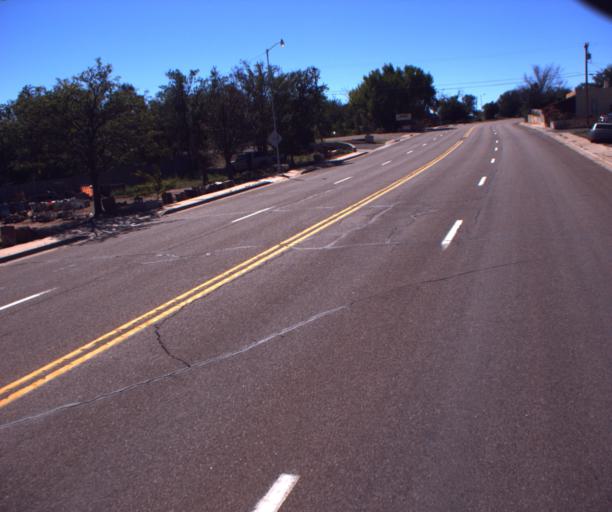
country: US
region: Arizona
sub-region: Apache County
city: Saint Johns
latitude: 34.5050
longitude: -109.3613
